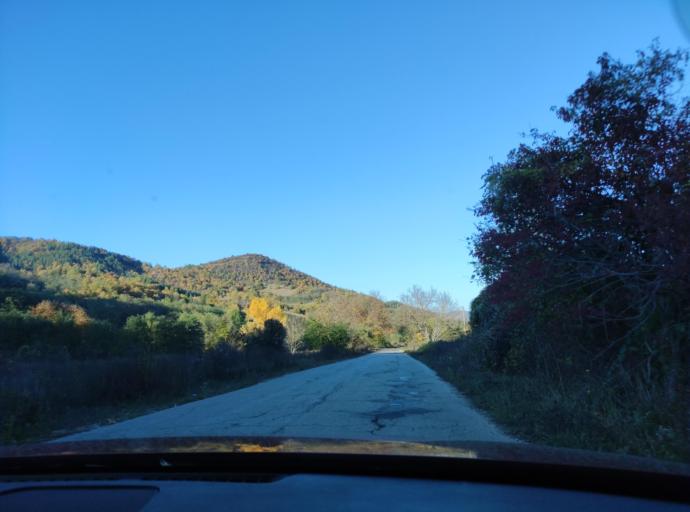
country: BG
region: Montana
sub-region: Obshtina Chiprovtsi
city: Chiprovtsi
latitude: 43.3929
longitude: 22.9228
